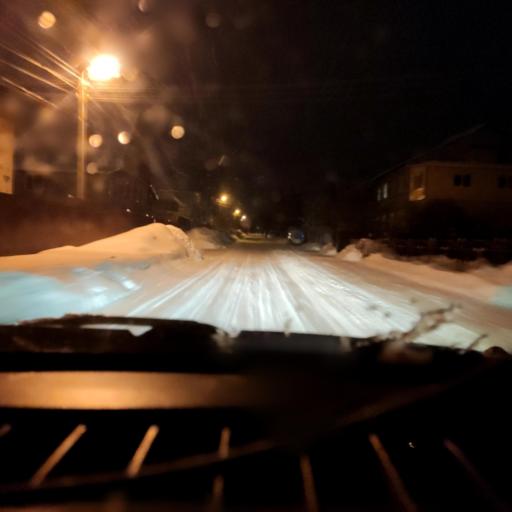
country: RU
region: Perm
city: Lobanovo
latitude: 57.8618
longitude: 56.2763
